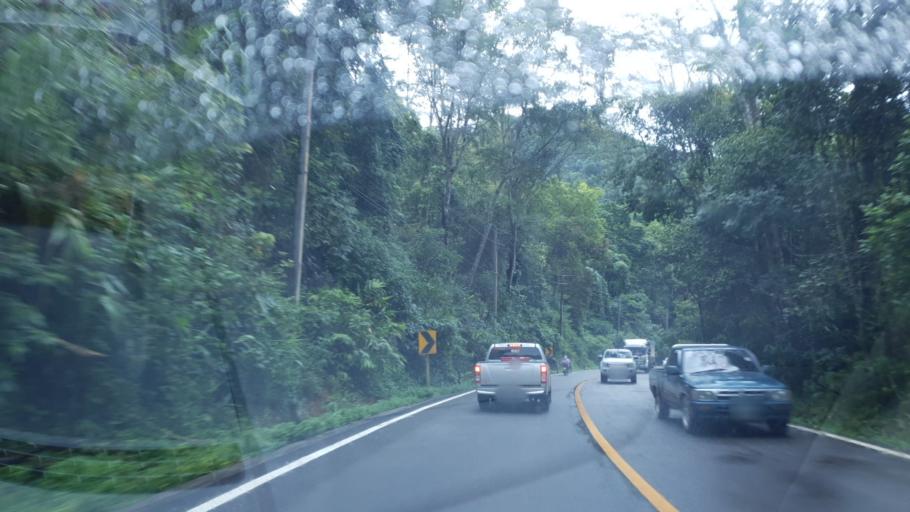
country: TH
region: Mae Hong Son
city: Ban Huai I Huak
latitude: 18.1482
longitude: 98.0933
